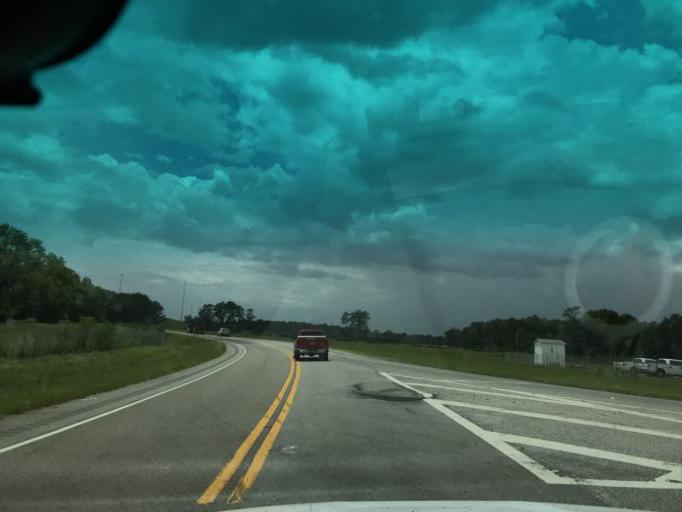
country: US
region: Alabama
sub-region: Montgomery County
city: Pike Road
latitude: 32.3705
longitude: -86.0771
